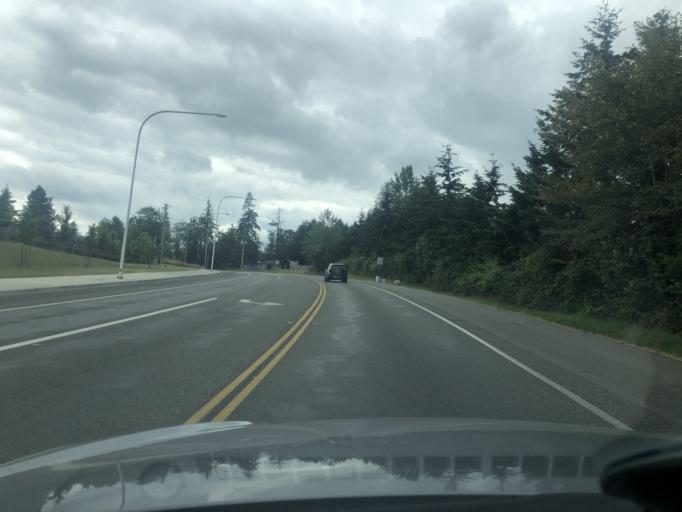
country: US
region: Washington
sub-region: King County
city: Lea Hill
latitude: 47.3297
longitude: -122.1647
